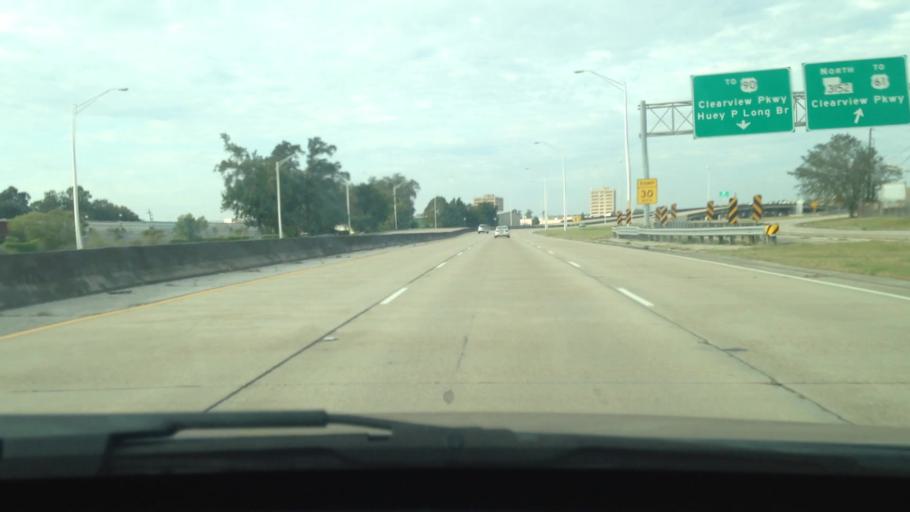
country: US
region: Louisiana
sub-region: Jefferson Parish
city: Metairie Terrace
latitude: 29.9698
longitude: -90.1784
